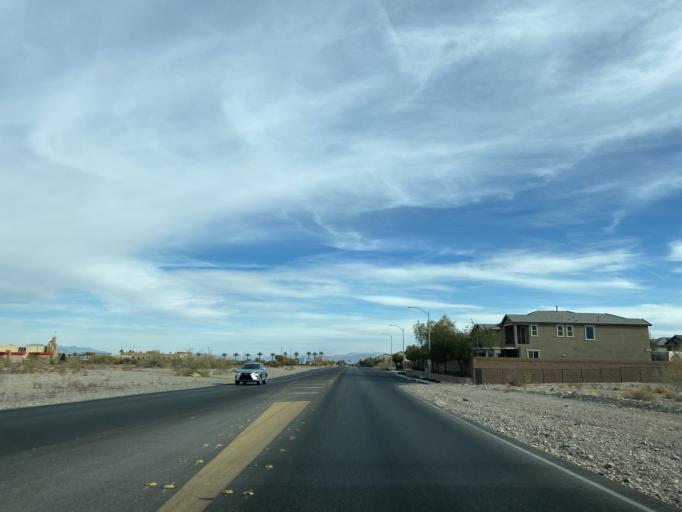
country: US
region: Nevada
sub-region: Clark County
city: Enterprise
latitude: 36.0409
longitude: -115.2687
